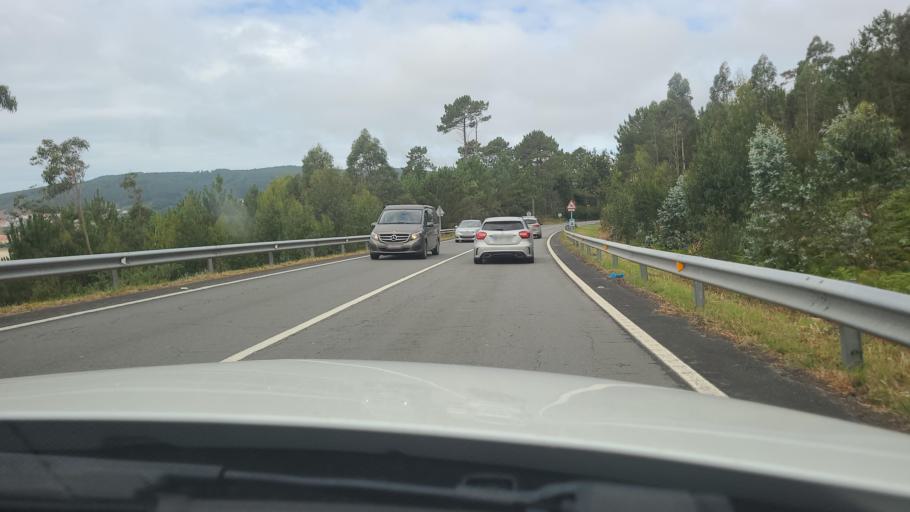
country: ES
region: Galicia
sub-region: Provincia da Coruna
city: Fisterra
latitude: 42.9273
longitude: -9.2478
